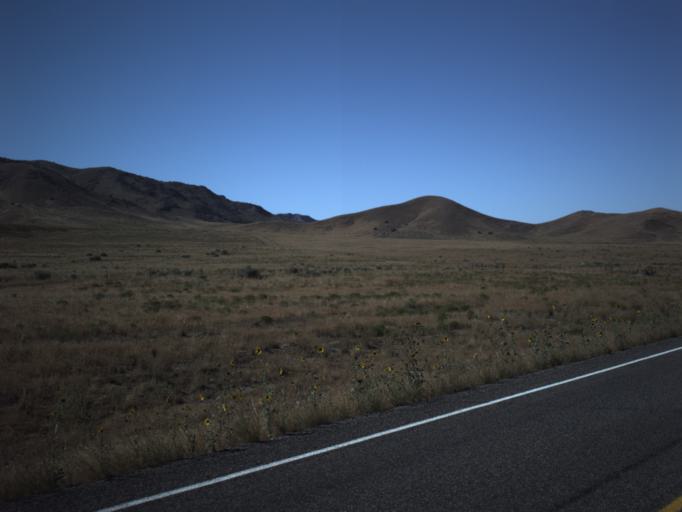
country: US
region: Utah
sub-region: Millard County
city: Delta
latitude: 39.6645
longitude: -112.2753
